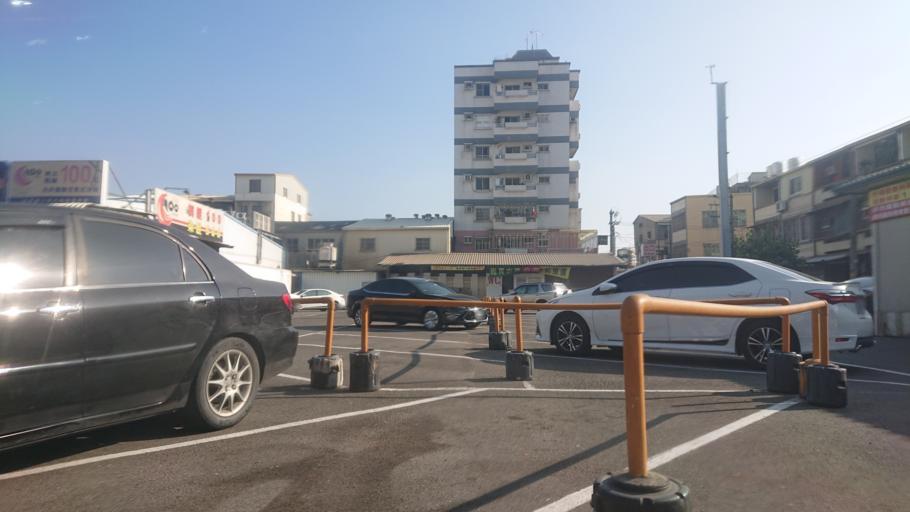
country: TW
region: Taiwan
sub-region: Tainan
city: Tainan
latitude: 23.0141
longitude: 120.2353
